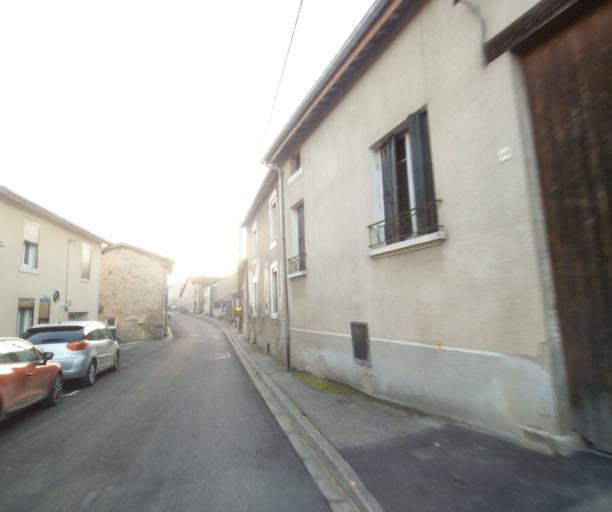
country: FR
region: Champagne-Ardenne
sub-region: Departement de la Haute-Marne
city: Bienville
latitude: 48.6044
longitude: 5.0354
